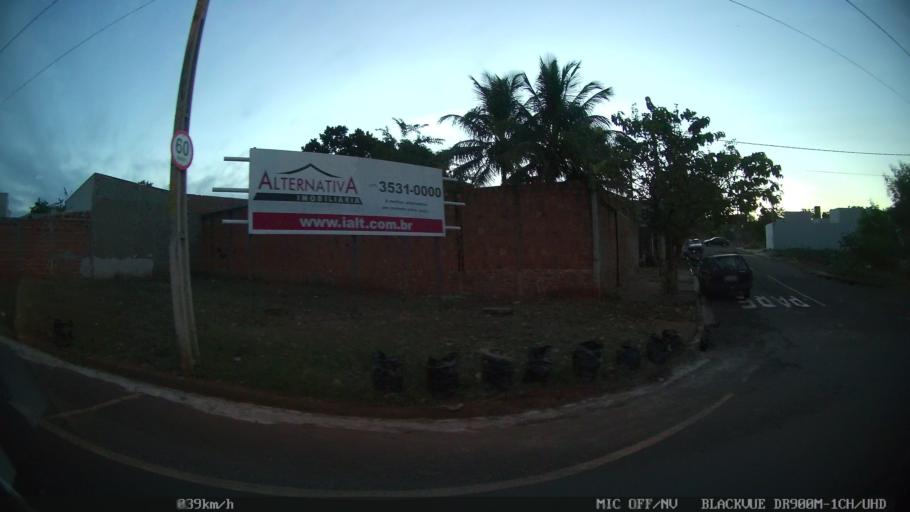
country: BR
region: Sao Paulo
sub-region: Catanduva
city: Catanduva
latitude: -21.1424
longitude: -48.9903
